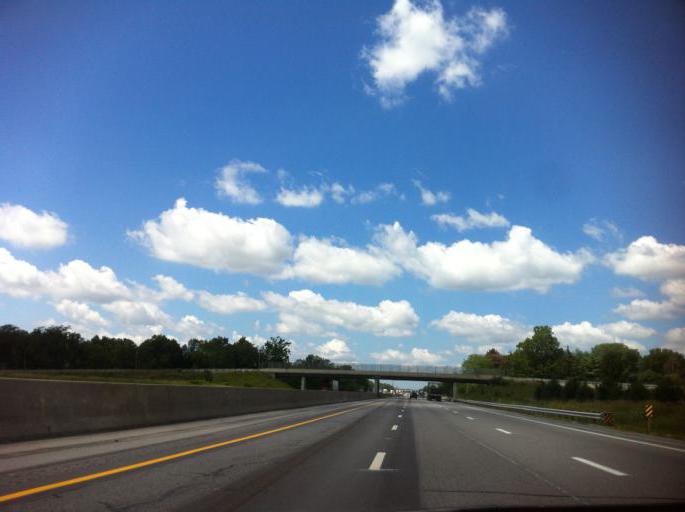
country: US
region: Ohio
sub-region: Ottawa County
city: Elmore
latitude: 41.4667
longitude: -83.3045
